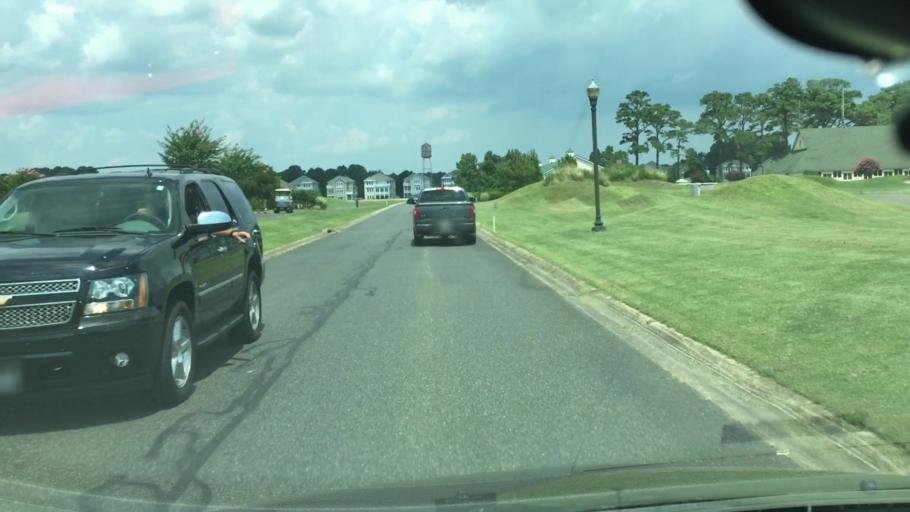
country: US
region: Maryland
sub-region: Worcester County
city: Ocean Pines
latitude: 38.3481
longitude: -75.1522
